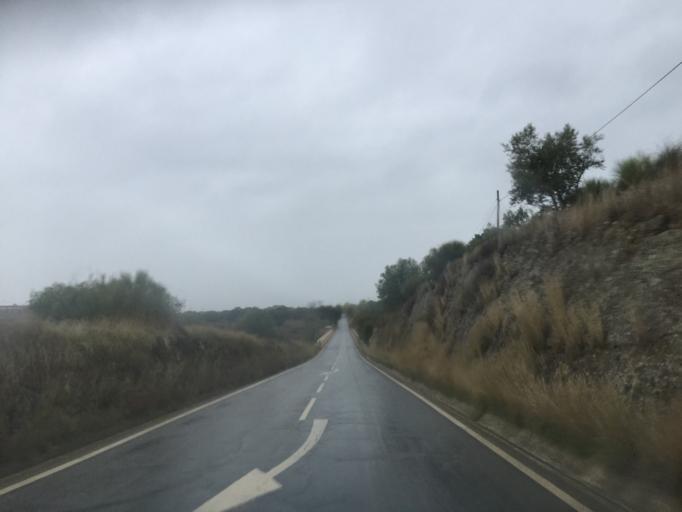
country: PT
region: Portalegre
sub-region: Avis
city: Avis
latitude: 39.0666
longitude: -7.8993
